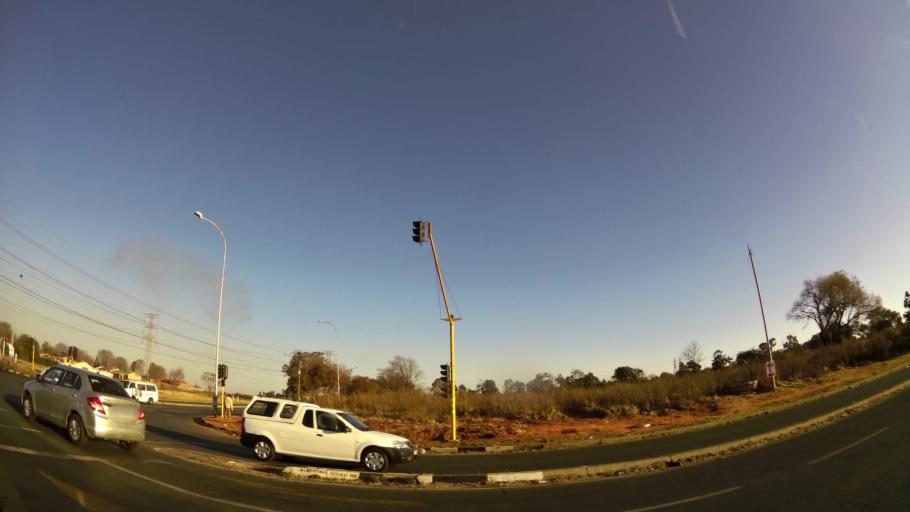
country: ZA
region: Gauteng
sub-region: City of Johannesburg Metropolitan Municipality
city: Roodepoort
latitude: -26.1797
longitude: 27.9010
